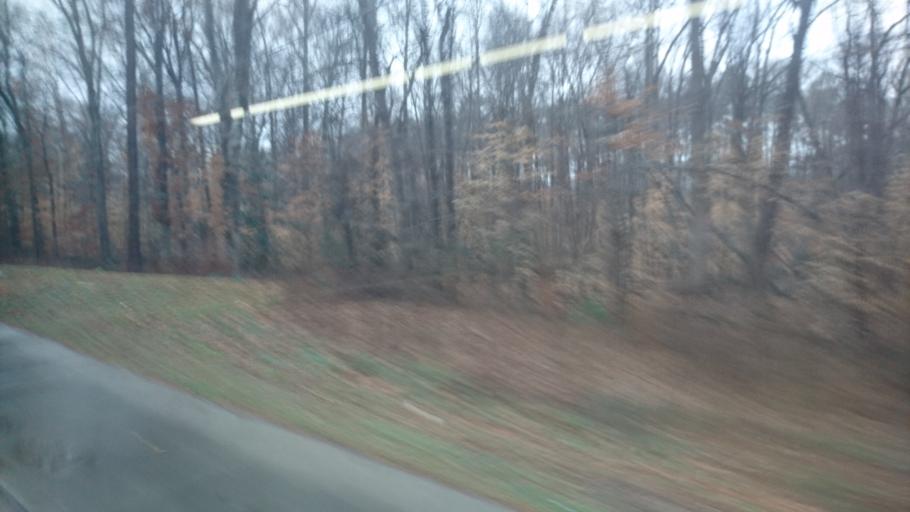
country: US
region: North Carolina
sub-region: Durham County
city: Durham
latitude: 36.0007
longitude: -78.9522
